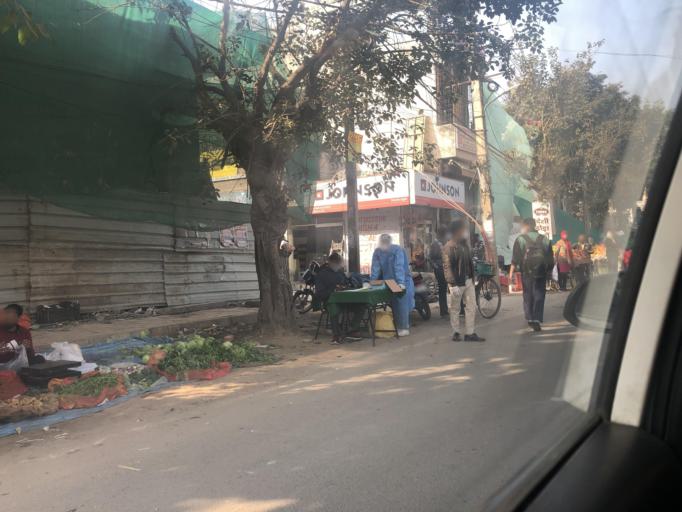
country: IN
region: Haryana
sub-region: Jhajjar
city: Bahadurgarh
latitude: 28.6147
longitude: 76.9776
